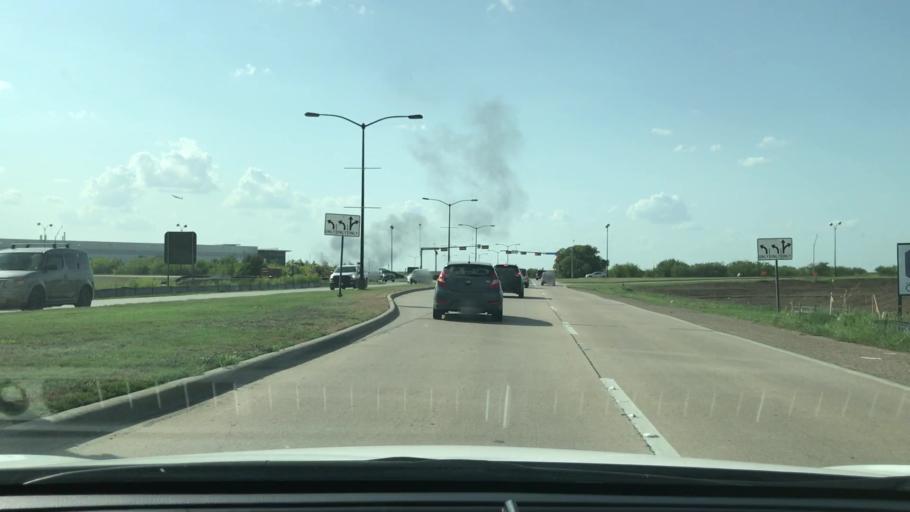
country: US
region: Texas
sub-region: Tarrant County
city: Euless
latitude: 32.8678
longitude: -97.0163
